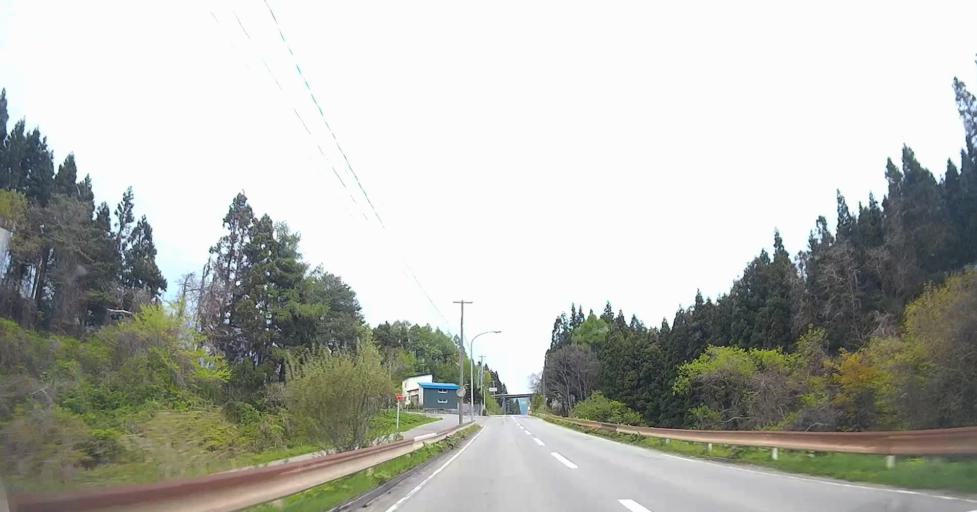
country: JP
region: Aomori
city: Goshogawara
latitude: 41.1774
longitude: 140.4829
